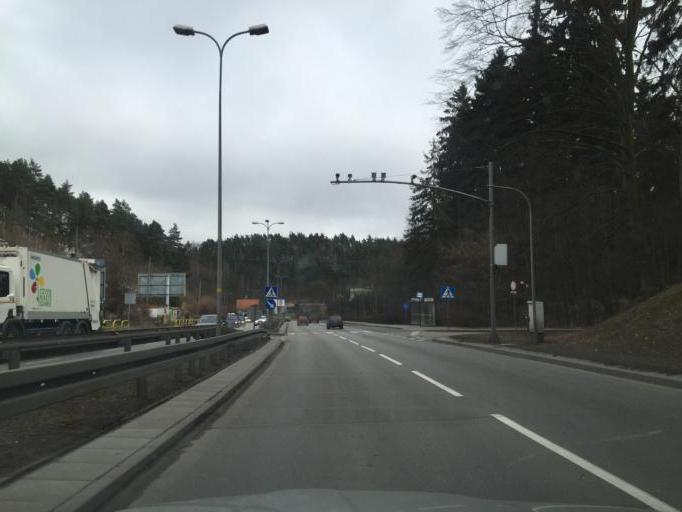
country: PL
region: Pomeranian Voivodeship
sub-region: Powiat gdanski
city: Kowale
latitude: 54.3709
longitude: 18.5553
